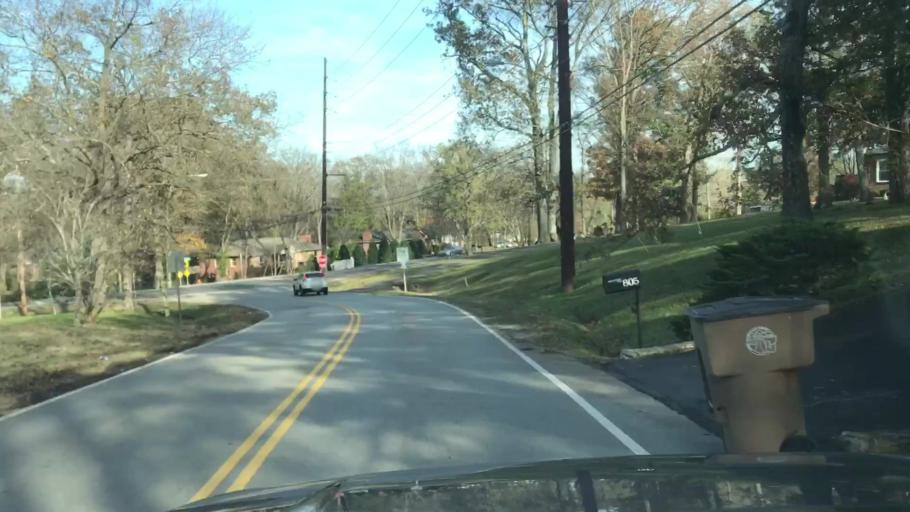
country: US
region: Tennessee
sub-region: Davidson County
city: Belle Meade
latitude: 36.1176
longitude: -86.8924
